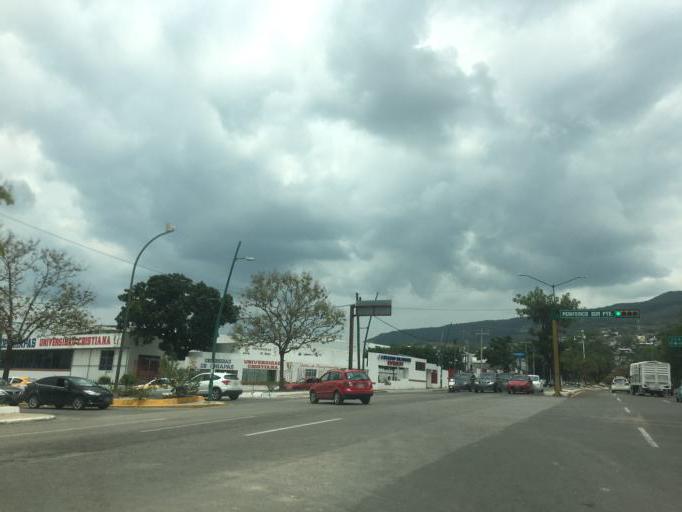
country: MX
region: Chiapas
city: Tuxtla Gutierrez
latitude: 16.7508
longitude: -93.1416
